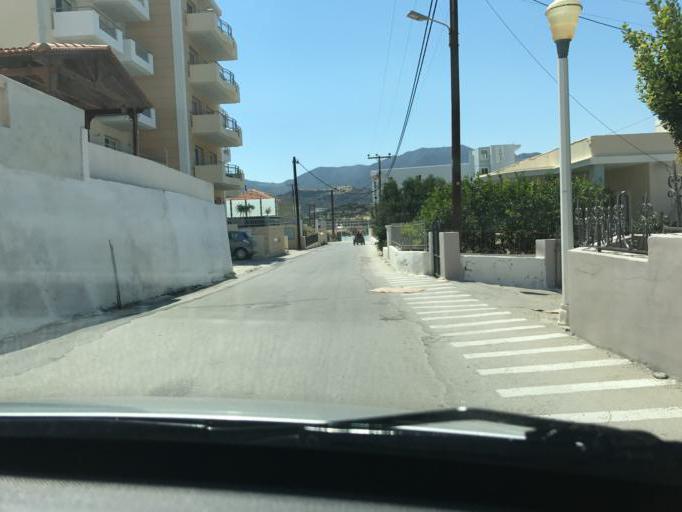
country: GR
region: South Aegean
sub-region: Nomos Dodekanisou
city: Karpathos
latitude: 35.5075
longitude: 27.2079
